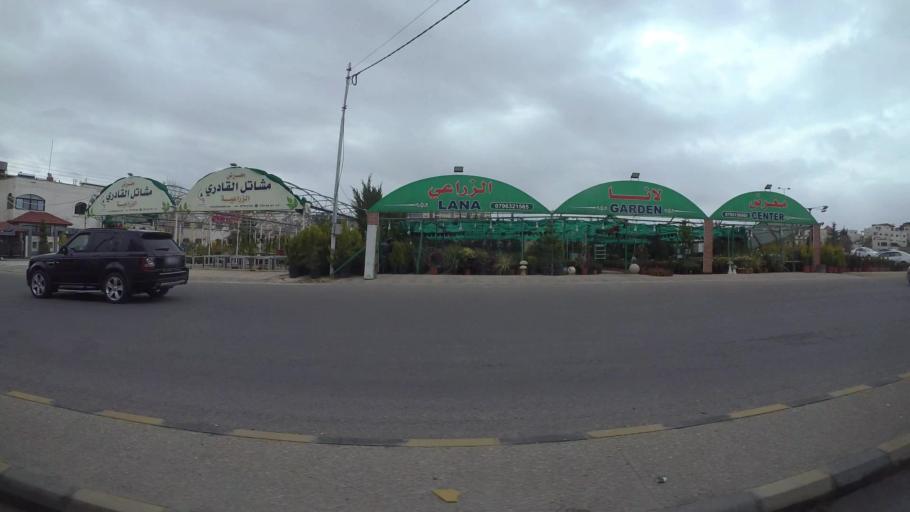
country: JO
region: Amman
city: Wadi as Sir
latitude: 31.9830
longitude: 35.8382
